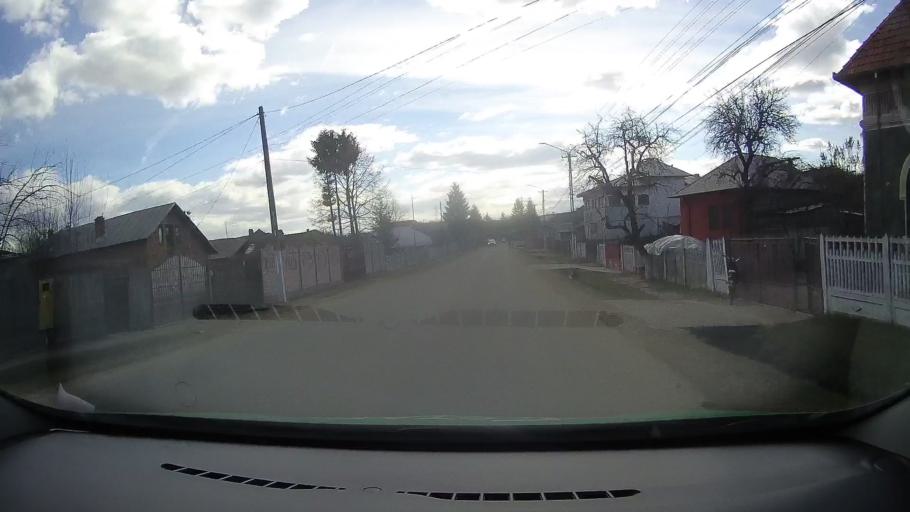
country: RO
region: Dambovita
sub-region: Comuna Doicesti
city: Doicesti
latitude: 44.9765
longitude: 25.3921
